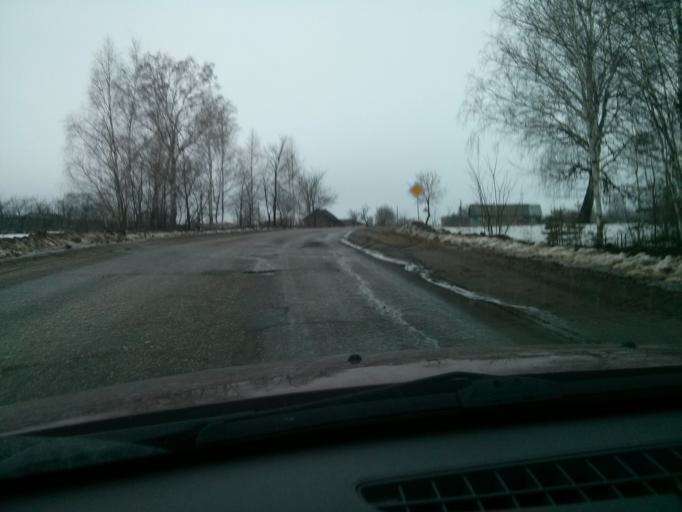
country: RU
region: Vladimir
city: Murom
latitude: 55.4606
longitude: 41.9787
